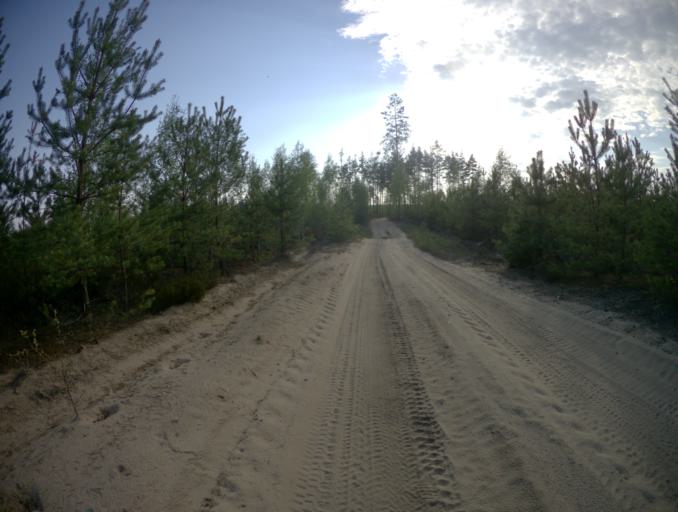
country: RU
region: Vladimir
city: Vyazniki
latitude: 56.4056
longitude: 42.1865
